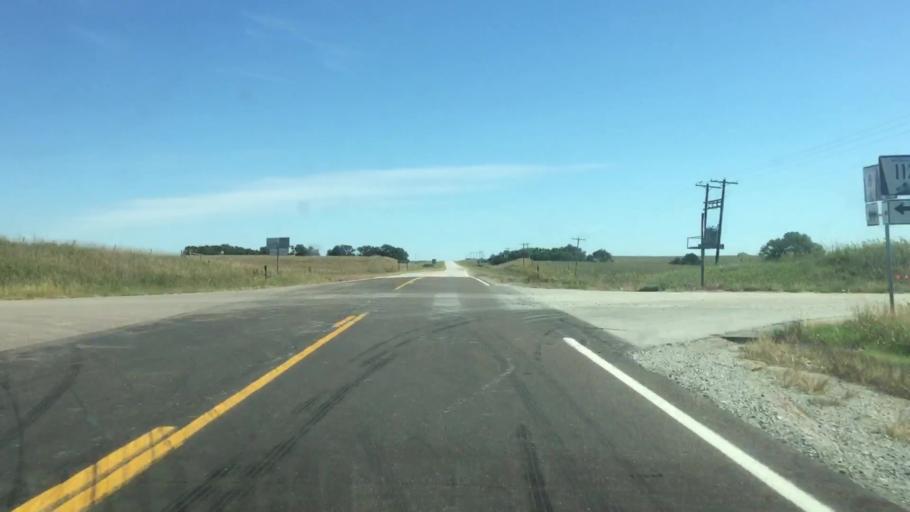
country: US
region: Nebraska
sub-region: Gage County
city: Wymore
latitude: 40.0455
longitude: -96.7461
